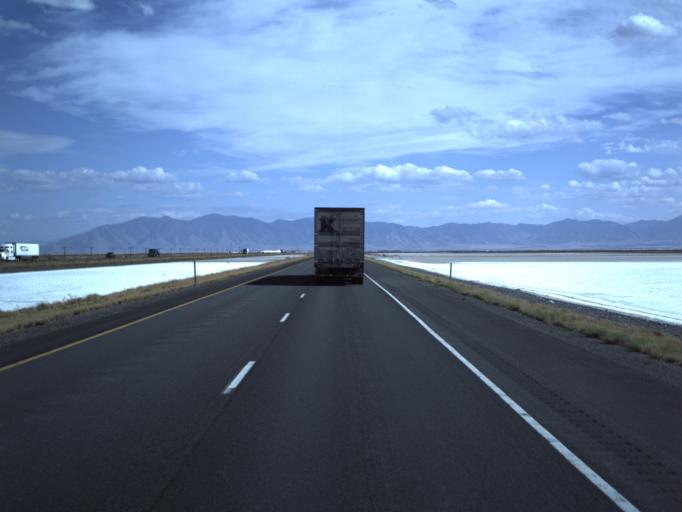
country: US
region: Utah
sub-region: Tooele County
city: Grantsville
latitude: 40.7293
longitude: -112.5870
